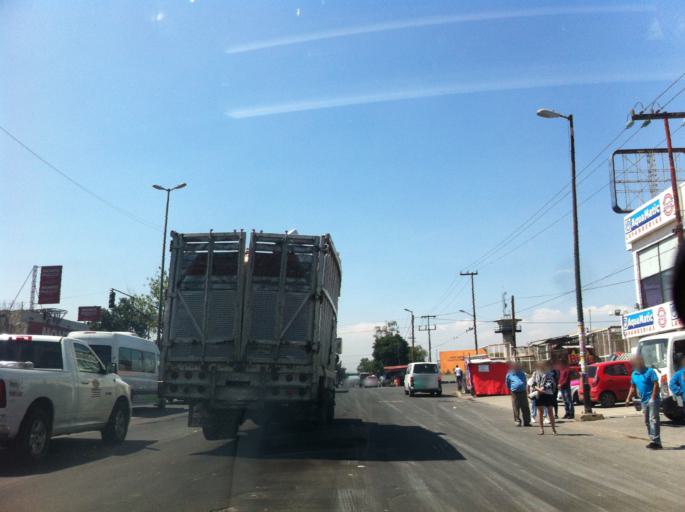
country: MX
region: Mexico
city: Los Reyes La Paz
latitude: 19.3553
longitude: -99.0084
